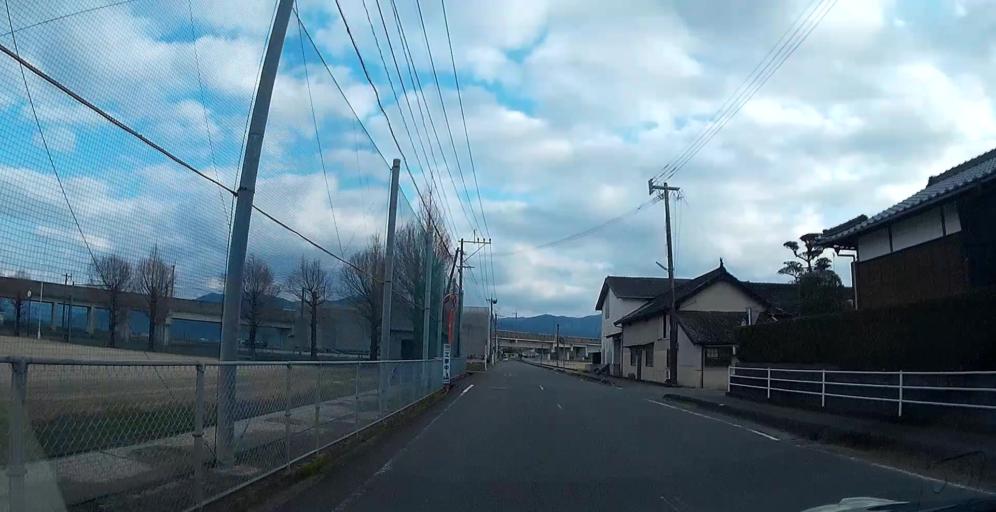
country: JP
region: Kumamoto
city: Yatsushiro
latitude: 32.5415
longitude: 130.6239
